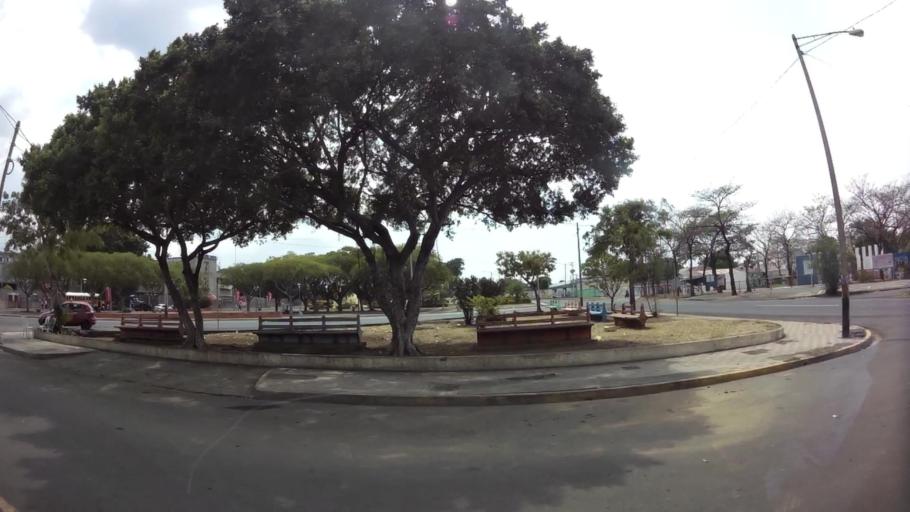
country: NI
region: Managua
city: Managua
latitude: 12.1509
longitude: -86.2819
